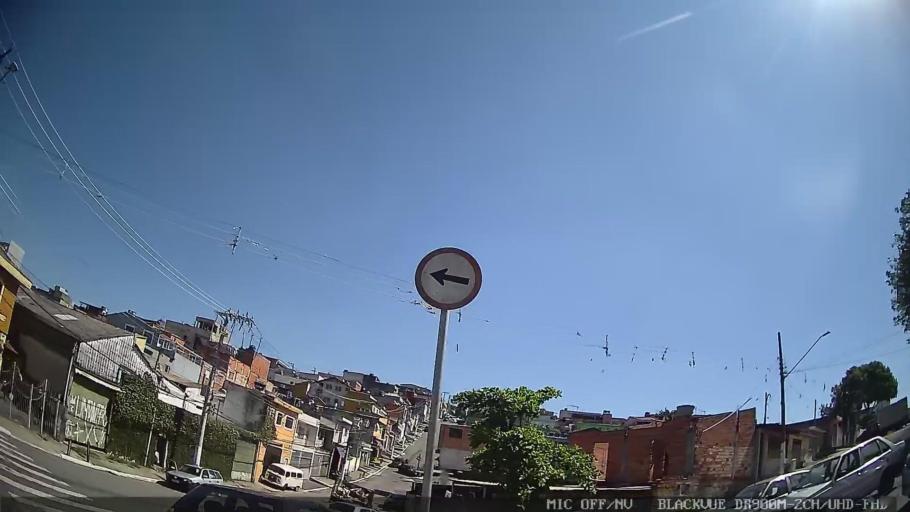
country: BR
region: Sao Paulo
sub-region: Sao Caetano Do Sul
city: Sao Caetano do Sul
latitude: -23.5912
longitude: -46.4969
